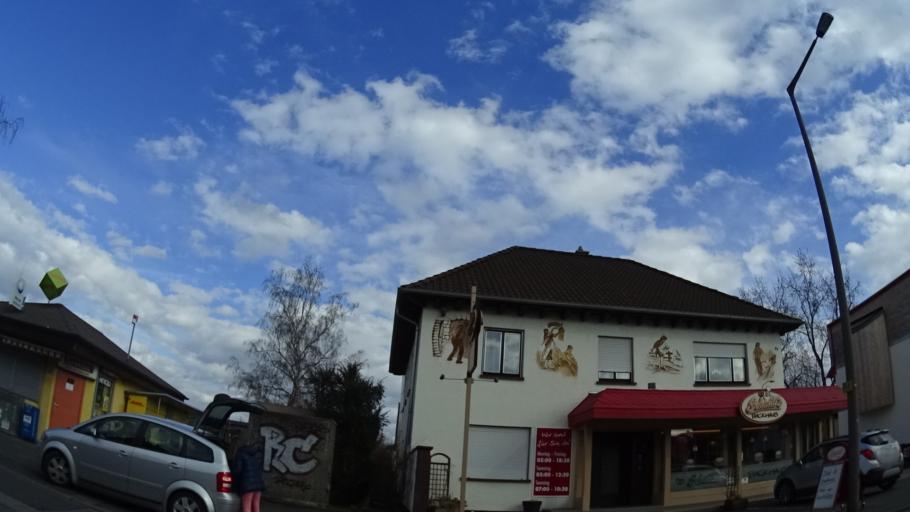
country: DE
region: Hesse
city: Lampertheim
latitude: 49.6014
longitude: 8.4691
